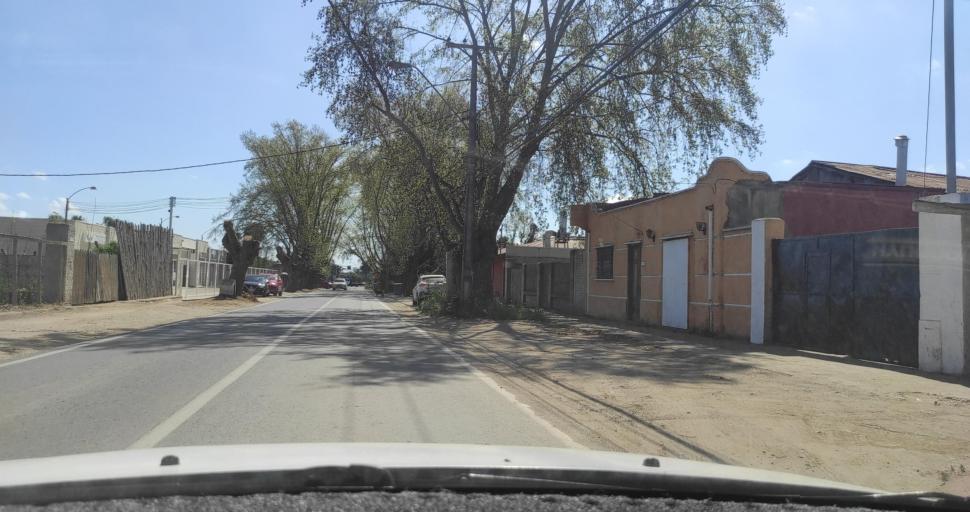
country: CL
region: Valparaiso
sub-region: Provincia de Marga Marga
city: Limache
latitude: -33.0093
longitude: -71.2484
